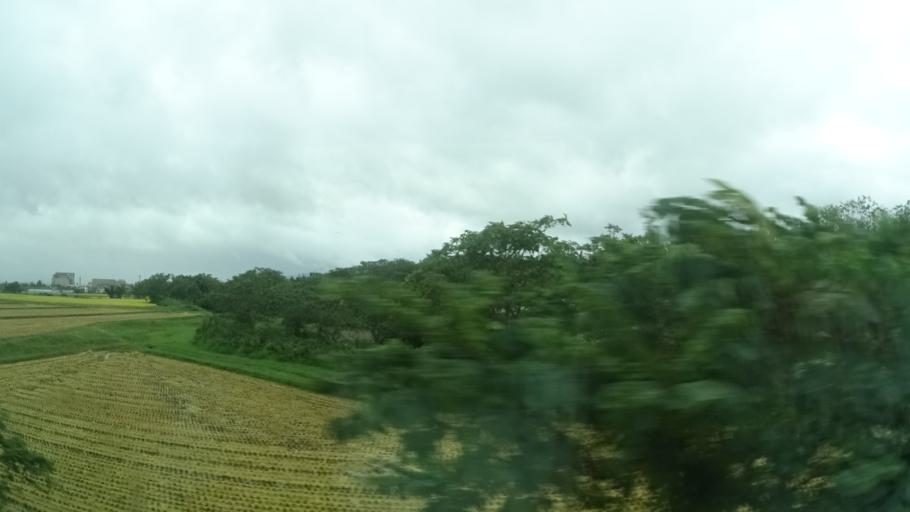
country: JP
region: Yamagata
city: Tsuruoka
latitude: 38.7423
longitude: 139.7908
